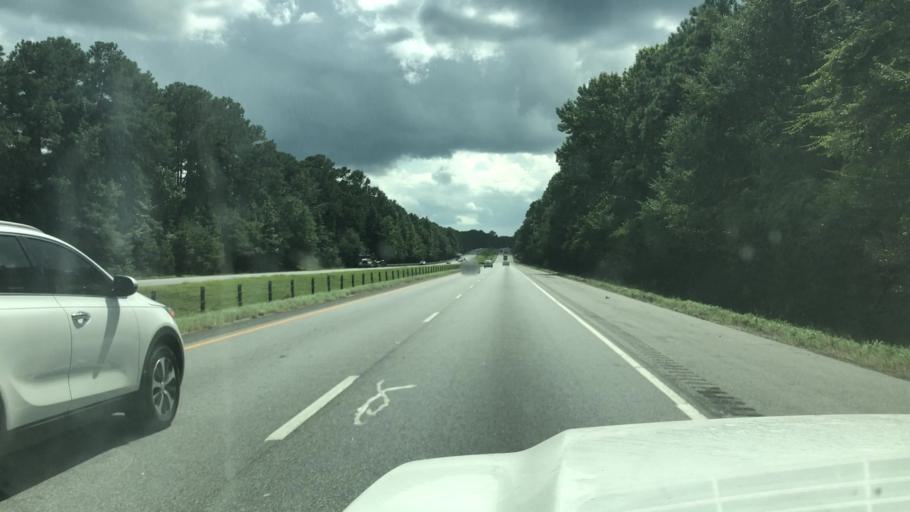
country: US
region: Alabama
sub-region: Lee County
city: Auburn
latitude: 32.5873
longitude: -85.4608
